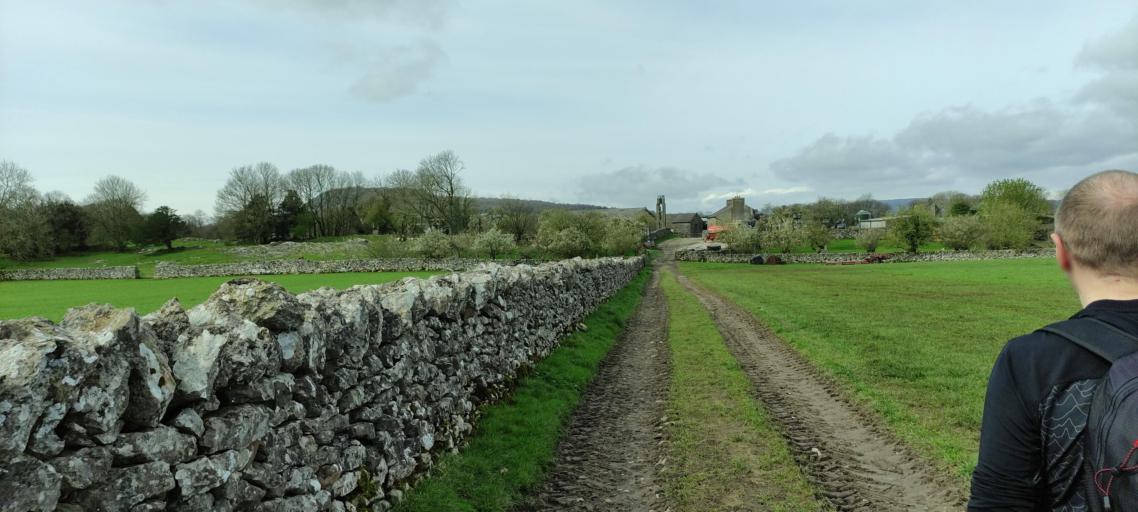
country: GB
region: England
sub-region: Cumbria
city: Arnside
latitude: 54.2022
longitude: -2.8003
